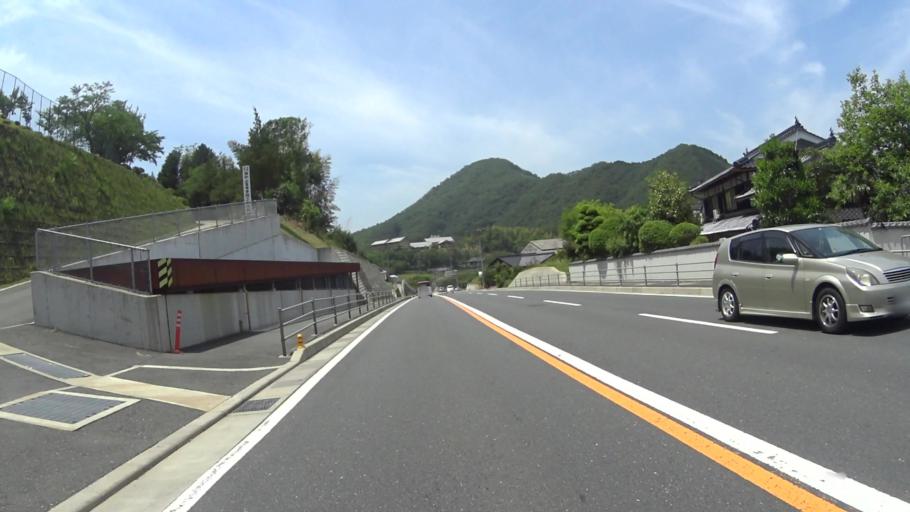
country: JP
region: Kyoto
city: Ayabe
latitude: 35.2205
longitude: 135.2272
